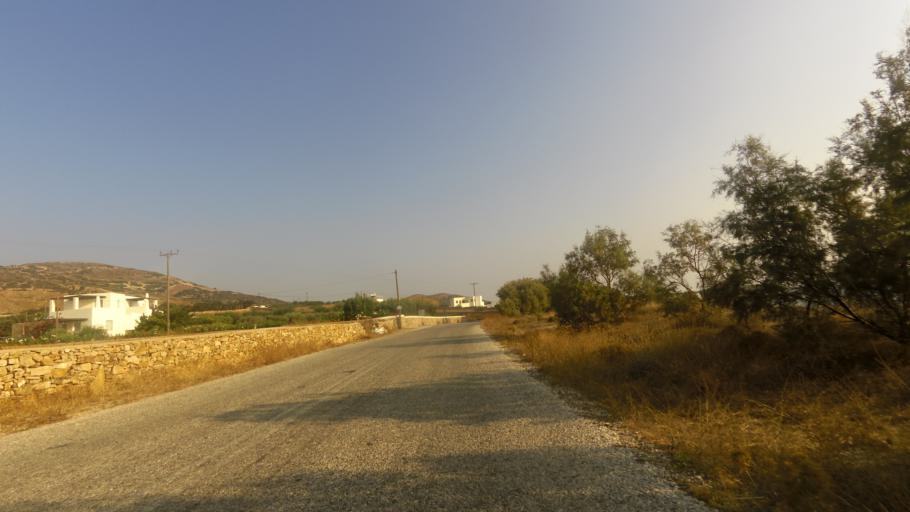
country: GR
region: South Aegean
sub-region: Nomos Kykladon
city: Antiparos
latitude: 37.0135
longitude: 25.0751
